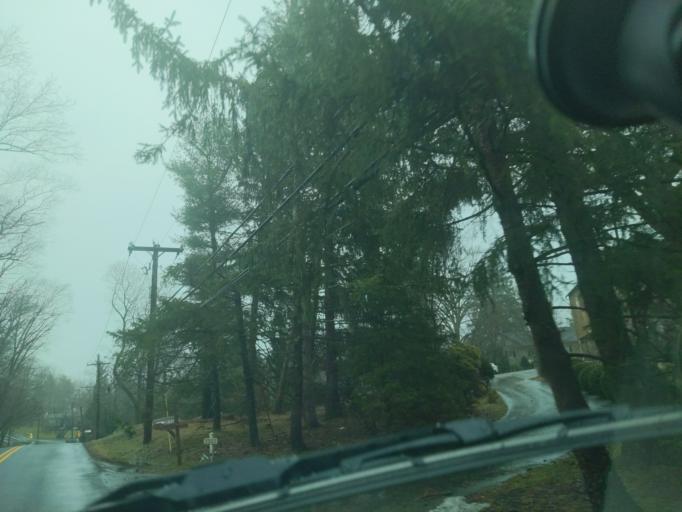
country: US
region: Pennsylvania
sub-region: Bucks County
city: Spinnerstown
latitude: 40.4371
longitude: -75.3943
